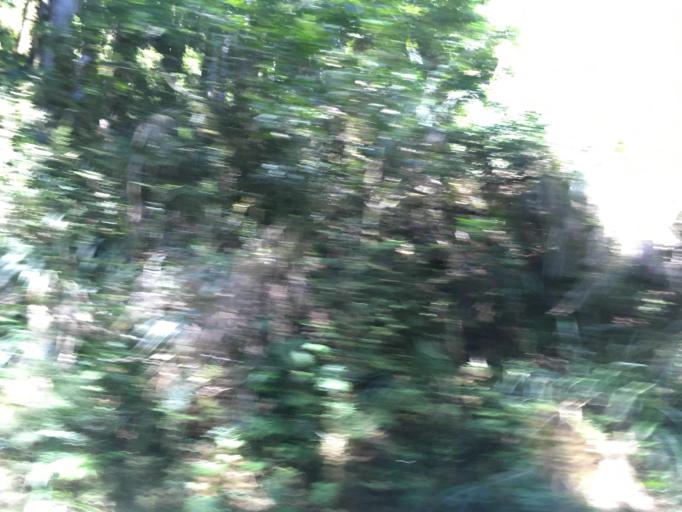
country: TW
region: Taiwan
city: Daxi
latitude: 24.5796
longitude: 121.4114
